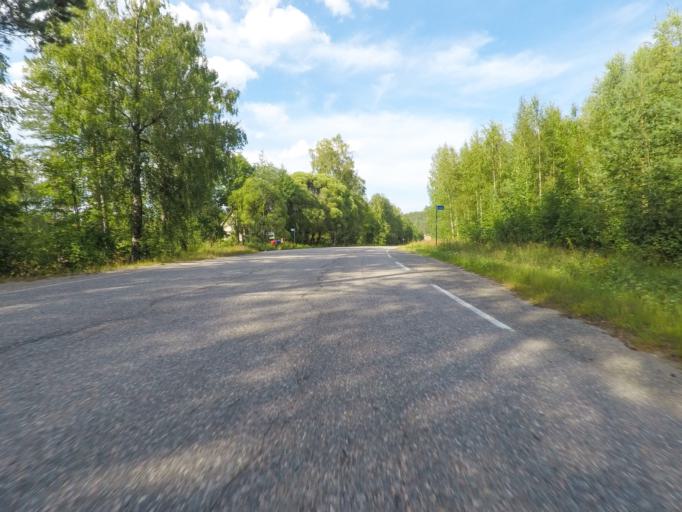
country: FI
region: Southern Savonia
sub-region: Mikkeli
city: Puumala
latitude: 61.6758
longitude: 28.2260
